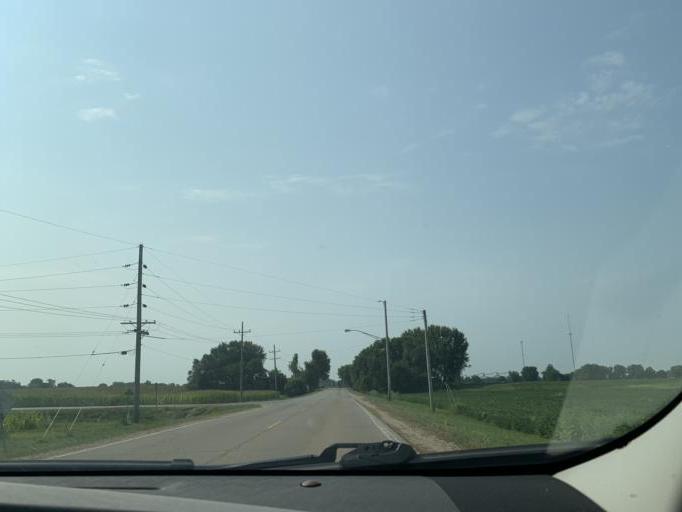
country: US
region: Illinois
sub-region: Whiteside County
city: Sterling
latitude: 41.8021
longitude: -89.7420
